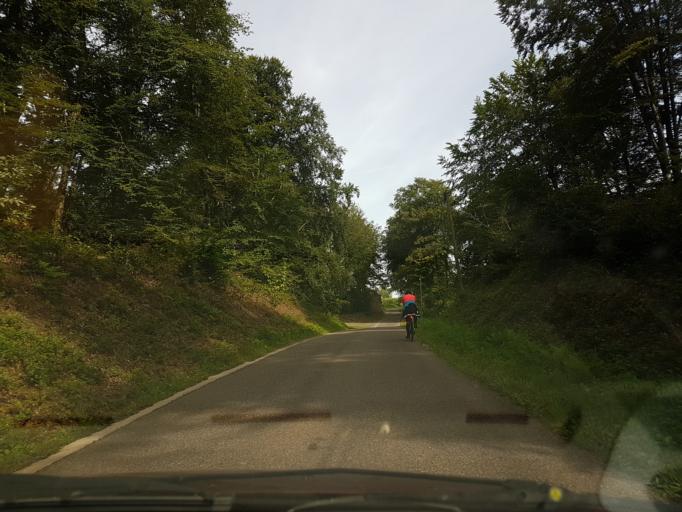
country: FR
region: Franche-Comte
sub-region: Departement de la Haute-Saone
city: Froideconche
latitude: 47.8634
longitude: 6.4751
